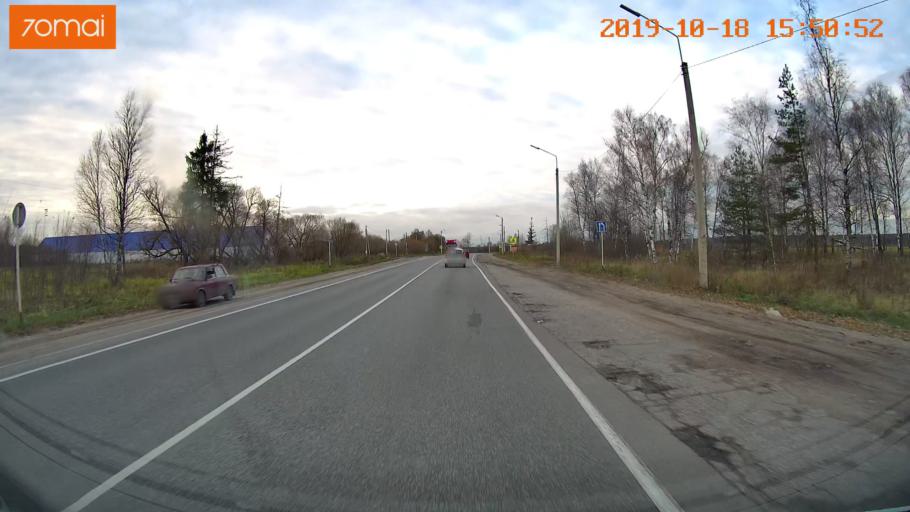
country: RU
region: Vladimir
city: Kommunar
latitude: 56.0367
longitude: 40.5546
